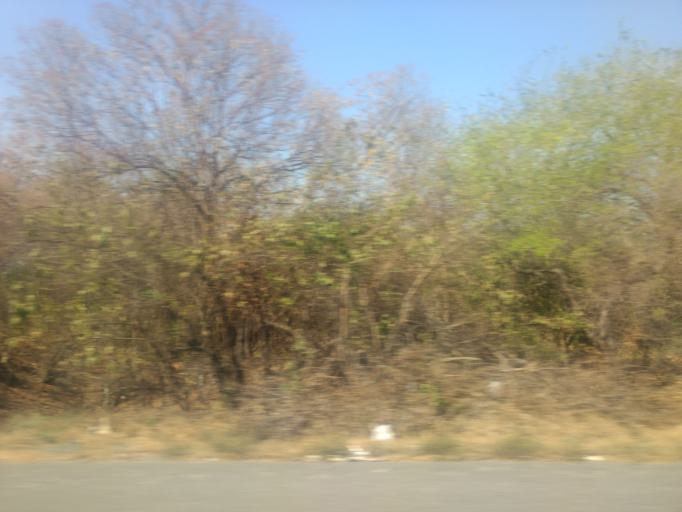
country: MX
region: Colima
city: El Colomo
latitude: 19.0337
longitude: -104.2534
